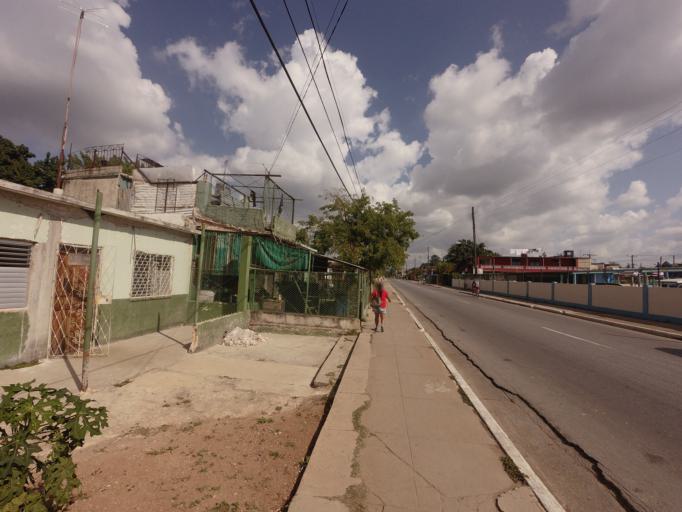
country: CU
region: Artemisa
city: Bauta
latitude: 22.9815
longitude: -82.5444
